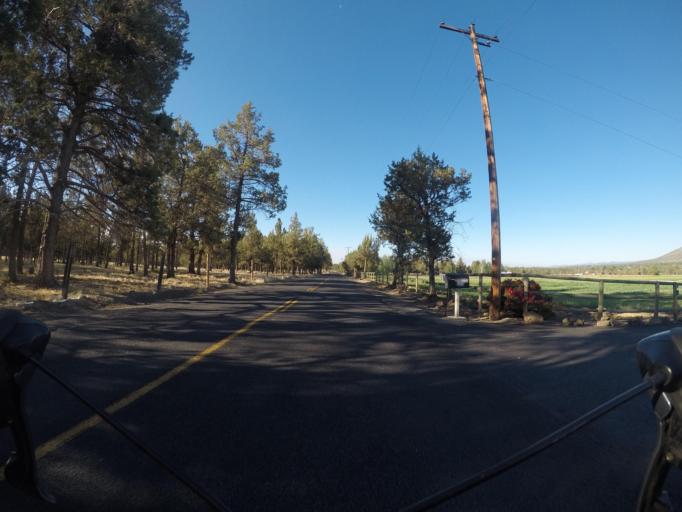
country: US
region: Oregon
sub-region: Deschutes County
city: Redmond
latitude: 44.2706
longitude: -121.2508
